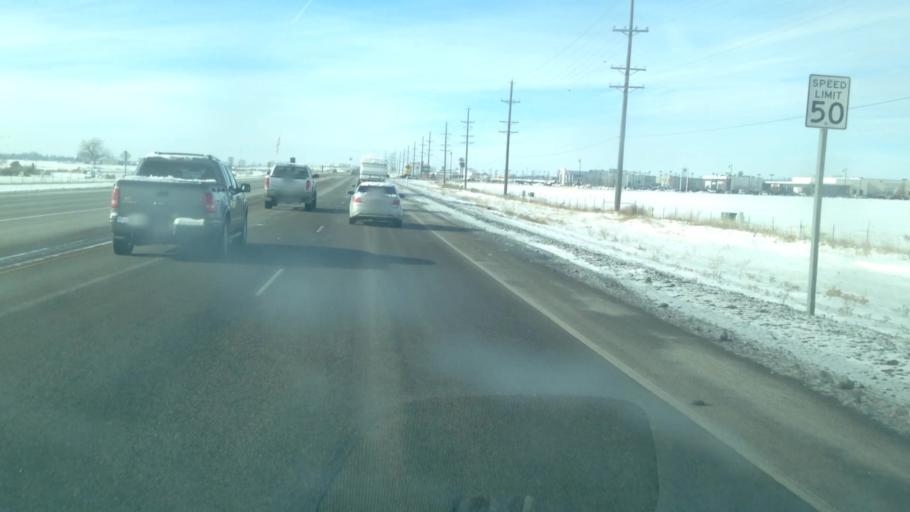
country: US
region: Idaho
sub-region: Bonneville County
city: Idaho Falls
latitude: 43.4678
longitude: -112.0691
